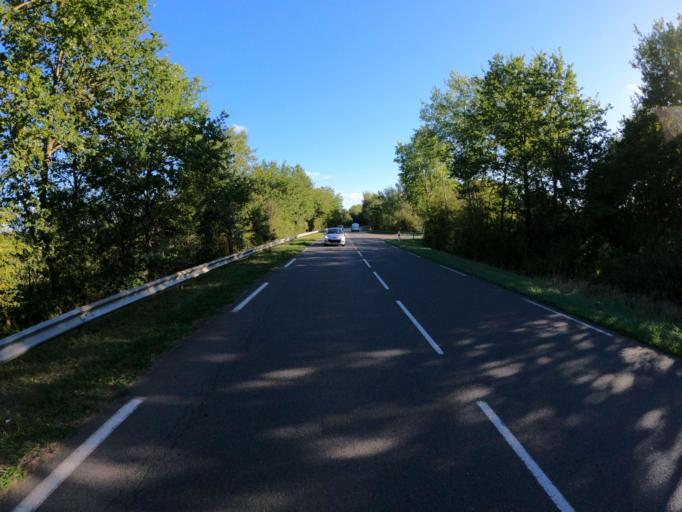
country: FR
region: Bourgogne
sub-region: Departement de Saone-et-Loire
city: Montchanin
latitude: 46.7411
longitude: 4.4452
